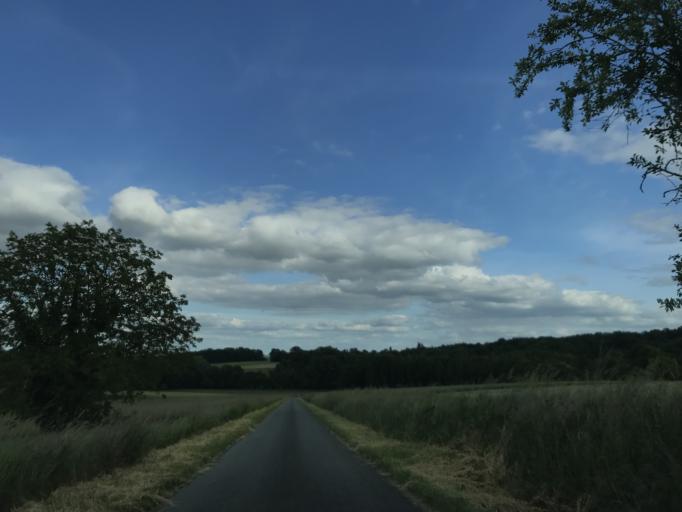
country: FR
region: Aquitaine
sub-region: Departement de la Dordogne
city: Saint-Aulaye
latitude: 45.2672
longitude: 0.1193
